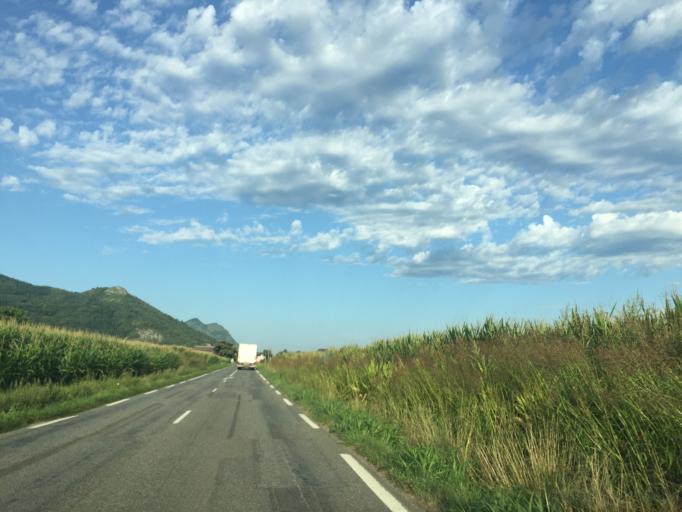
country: FR
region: Midi-Pyrenees
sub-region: Departement des Hautes-Pyrenees
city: Lourdes
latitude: 43.0947
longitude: -0.0027
